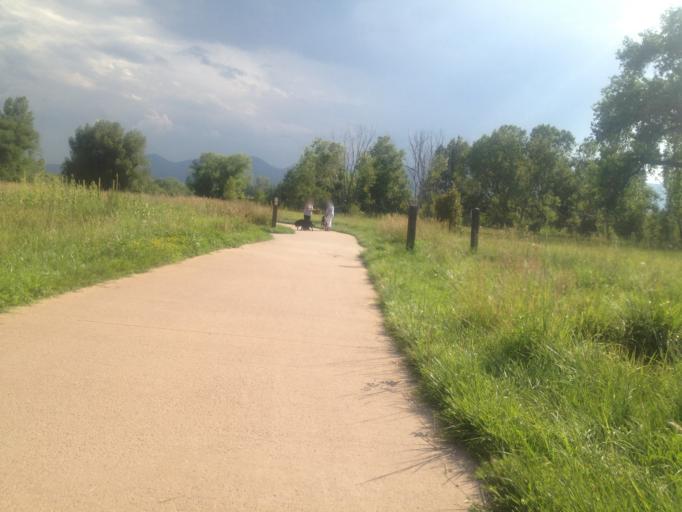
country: US
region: Colorado
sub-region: Boulder County
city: Boulder
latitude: 39.9931
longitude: -105.2167
